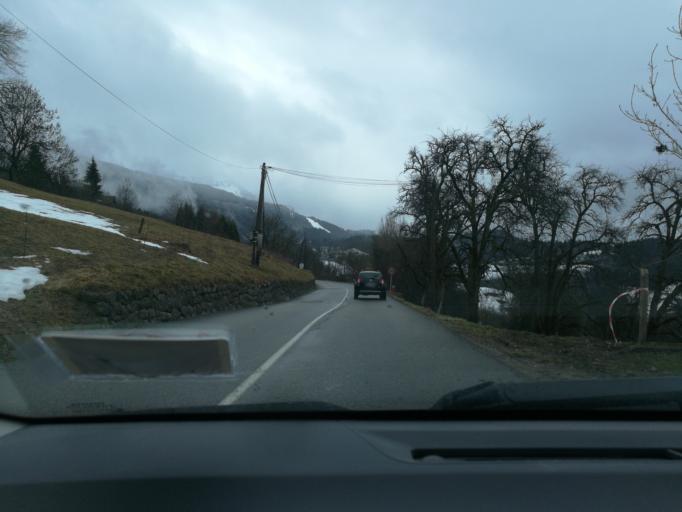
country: FR
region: Rhone-Alpes
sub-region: Departement de la Haute-Savoie
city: Araches-la-Frasse
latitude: 46.0550
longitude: 6.6305
